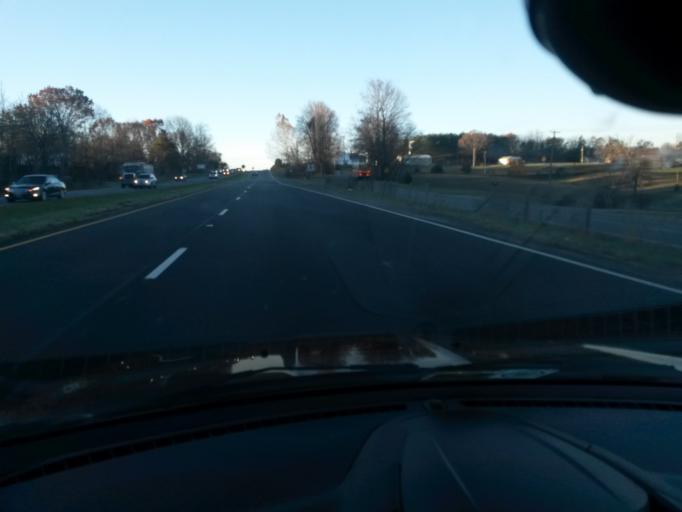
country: US
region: Virginia
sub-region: Franklin County
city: Henry Fork
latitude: 36.9612
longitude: -79.8755
